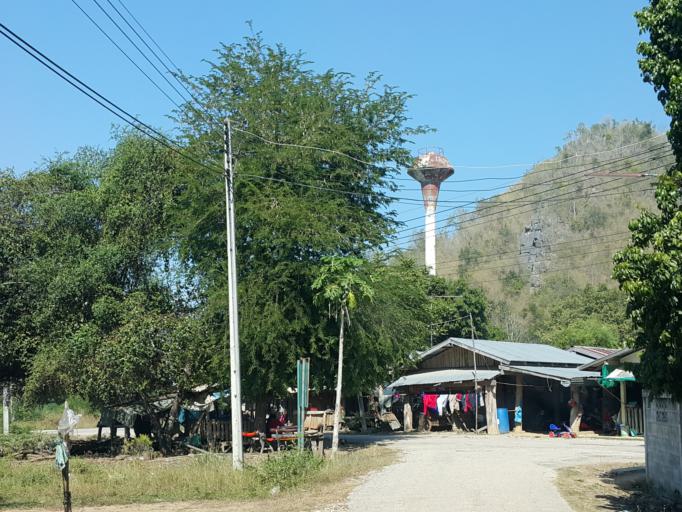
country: TH
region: Sukhothai
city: Thung Saliam
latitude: 17.3453
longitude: 99.4403
